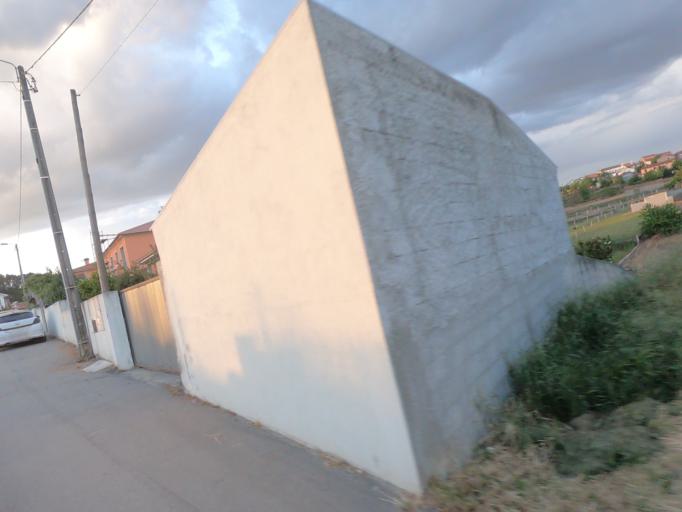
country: PT
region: Vila Real
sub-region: Vila Real
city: Vila Real
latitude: 41.2636
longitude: -7.6904
